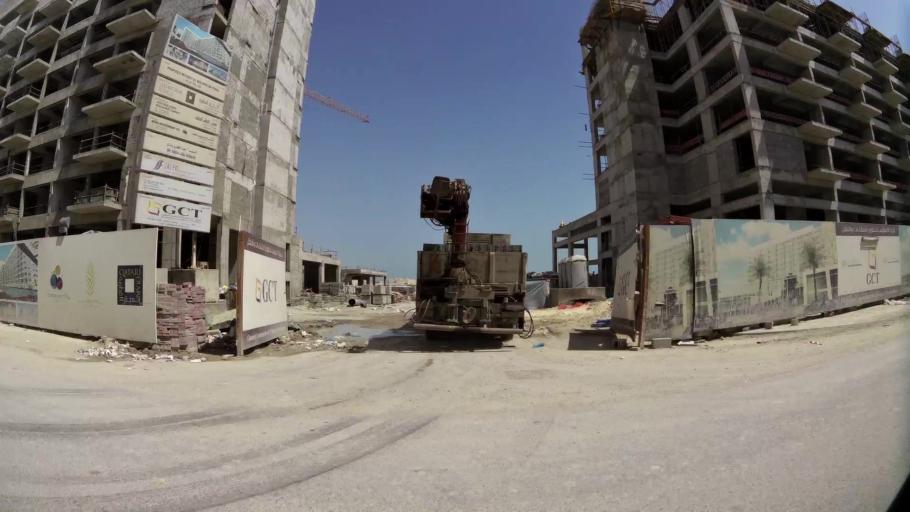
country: QA
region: Baladiyat Umm Salal
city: Umm Salal Muhammad
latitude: 25.4053
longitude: 51.5224
